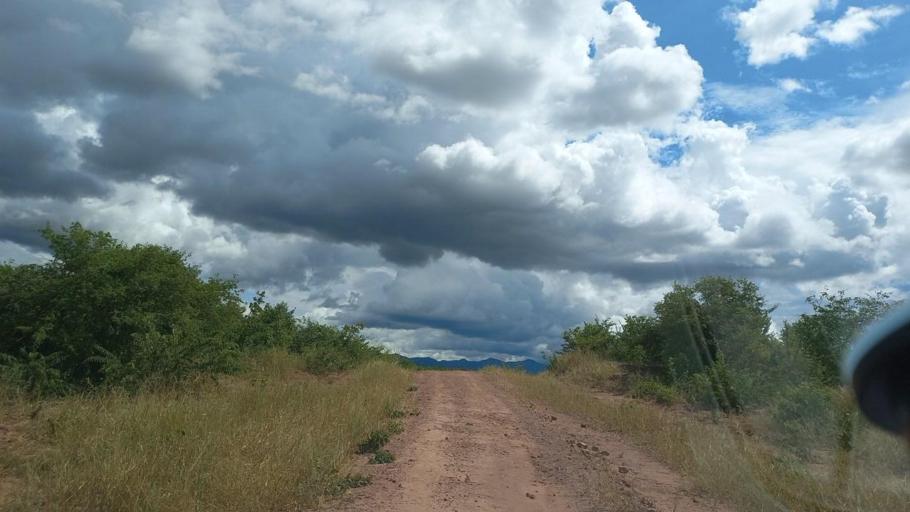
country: ZM
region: Lusaka
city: Luangwa
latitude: -15.6283
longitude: 30.3901
